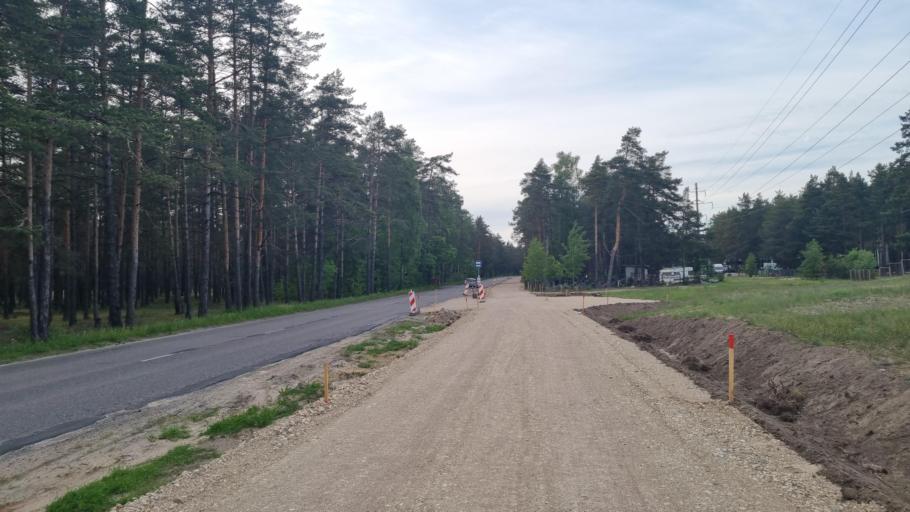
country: LV
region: Riga
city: Daugavgriva
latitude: 57.0164
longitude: 24.0182
